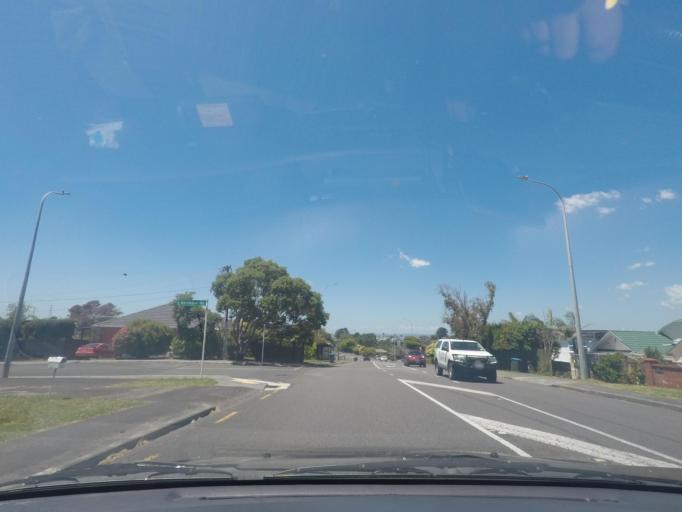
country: NZ
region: Auckland
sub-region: Auckland
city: Mangere
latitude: -36.9300
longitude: 174.7443
